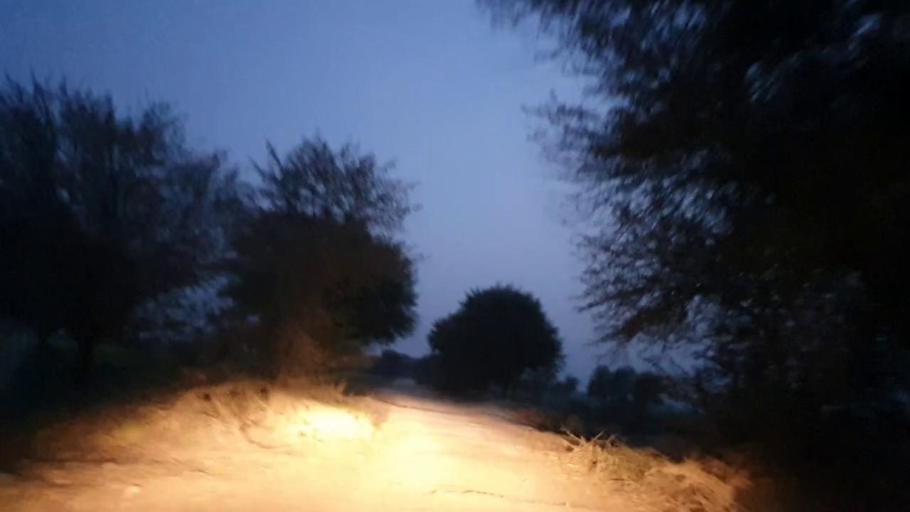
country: PK
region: Sindh
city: Tando Ghulam Ali
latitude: 25.0846
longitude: 68.9210
